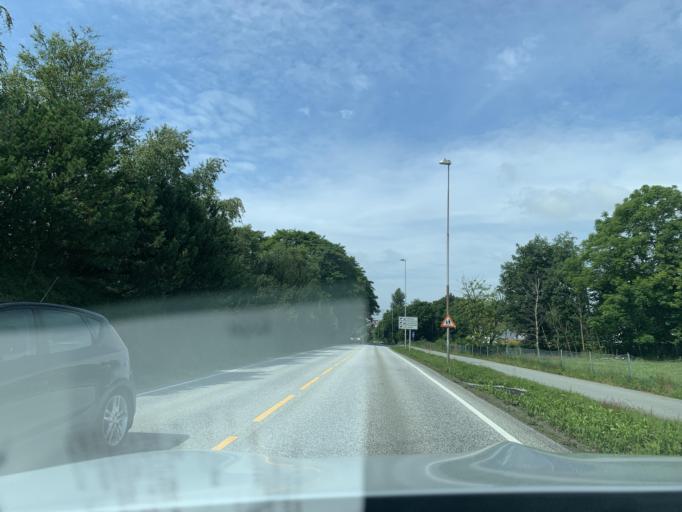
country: NO
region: Rogaland
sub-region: Sandnes
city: Sandnes
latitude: 58.8615
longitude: 5.7042
